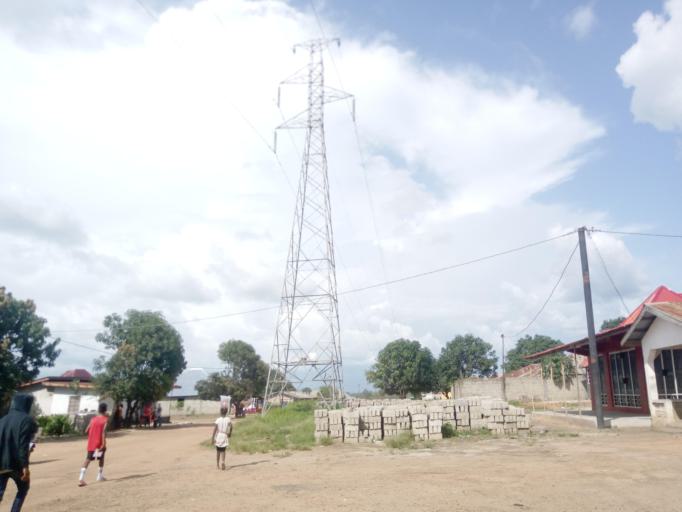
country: SL
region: Northern Province
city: Makeni
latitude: 8.9037
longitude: -12.0315
